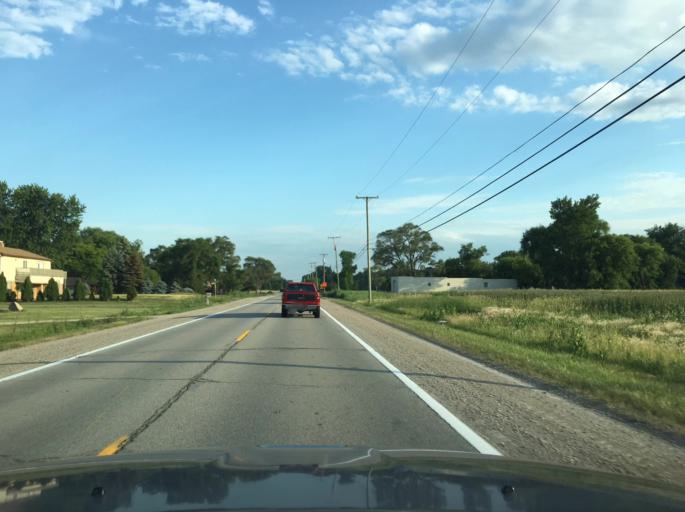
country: US
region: Michigan
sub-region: Macomb County
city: New Haven
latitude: 42.6977
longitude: -82.8788
